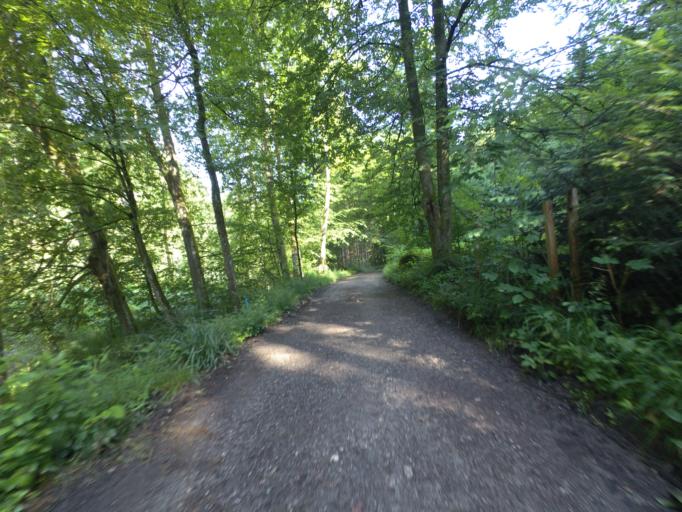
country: AT
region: Salzburg
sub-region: Politischer Bezirk Salzburg-Umgebung
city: Grodig
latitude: 47.7530
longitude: 12.9902
